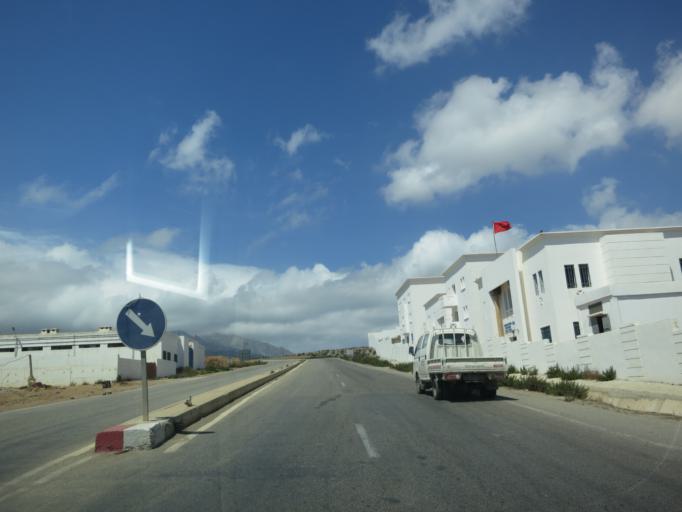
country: ES
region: Ceuta
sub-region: Ceuta
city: Ceuta
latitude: 35.8663
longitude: -5.3563
